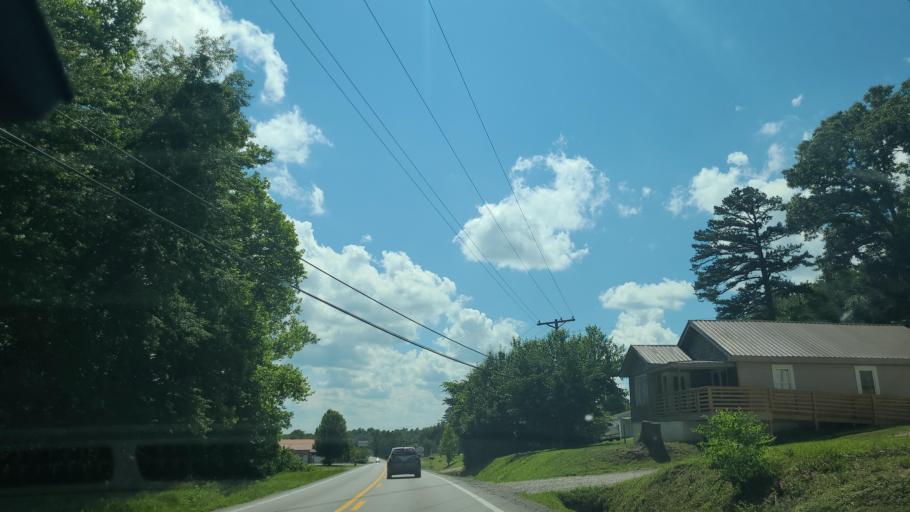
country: US
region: Kentucky
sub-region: Whitley County
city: Corbin
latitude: 36.9124
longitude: -84.1437
